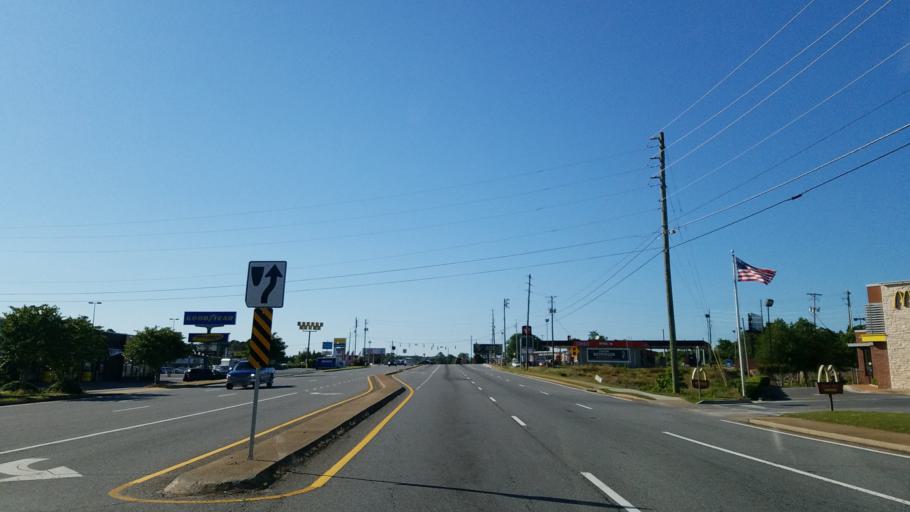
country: US
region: Georgia
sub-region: Cherokee County
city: Woodstock
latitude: 34.0859
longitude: -84.5760
